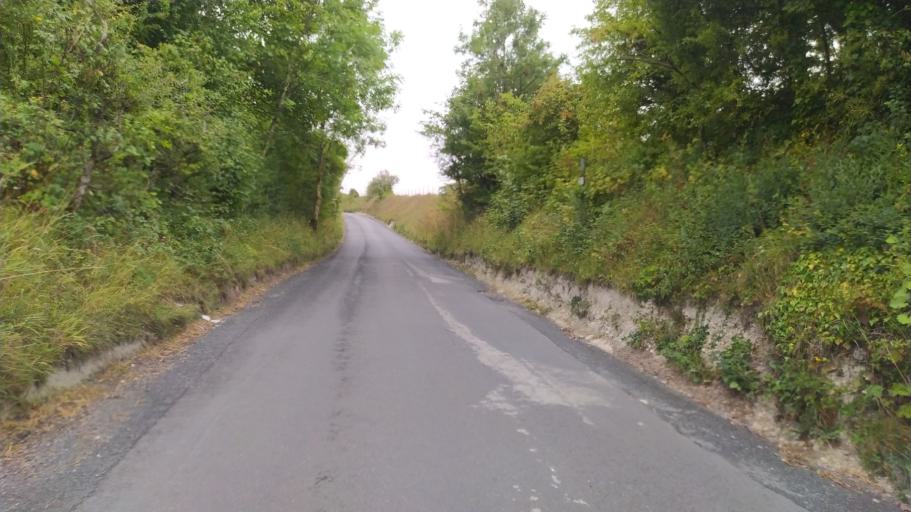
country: GB
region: England
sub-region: Wiltshire
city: Dinton
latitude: 51.0446
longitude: -1.9953
